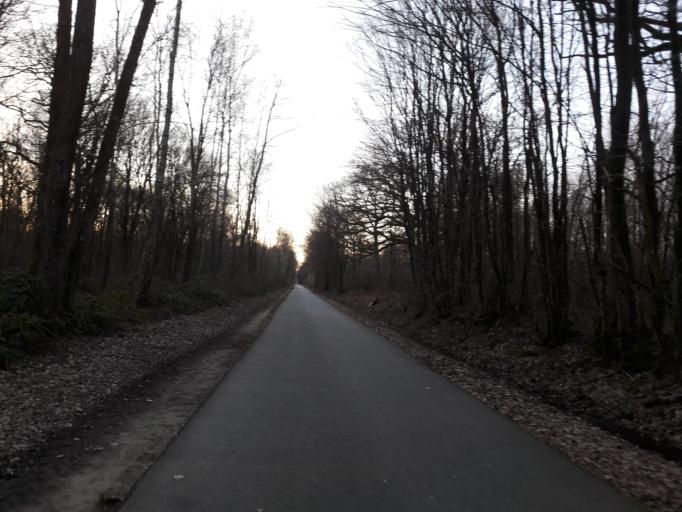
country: BE
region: Wallonia
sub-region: Province du Hainaut
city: Momignies
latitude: 50.0251
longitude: 4.2068
